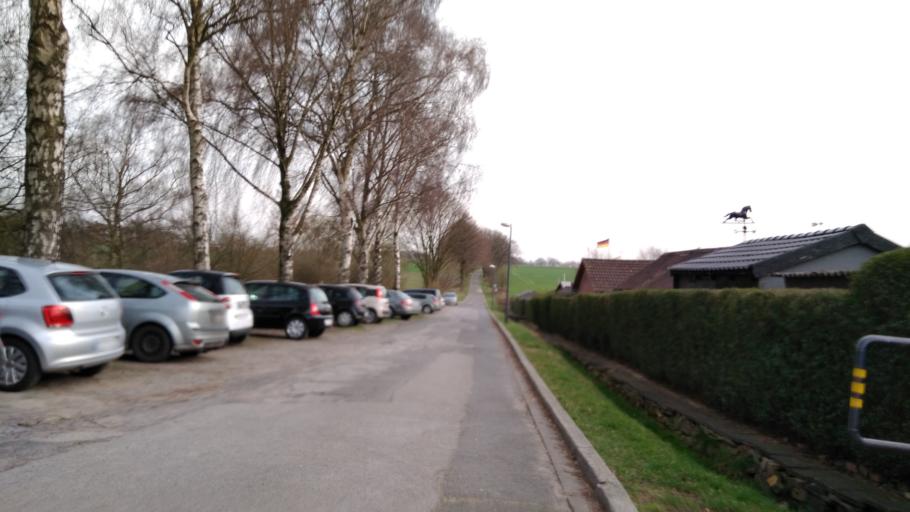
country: DE
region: North Rhine-Westphalia
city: Herten
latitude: 51.6048
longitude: 7.1163
